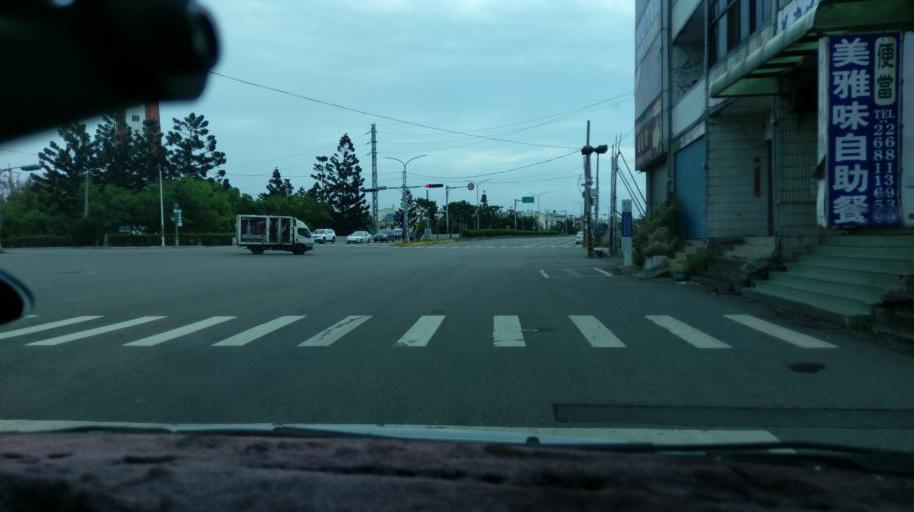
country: TW
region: Taiwan
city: Fengyuan
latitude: 24.4097
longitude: 120.6433
